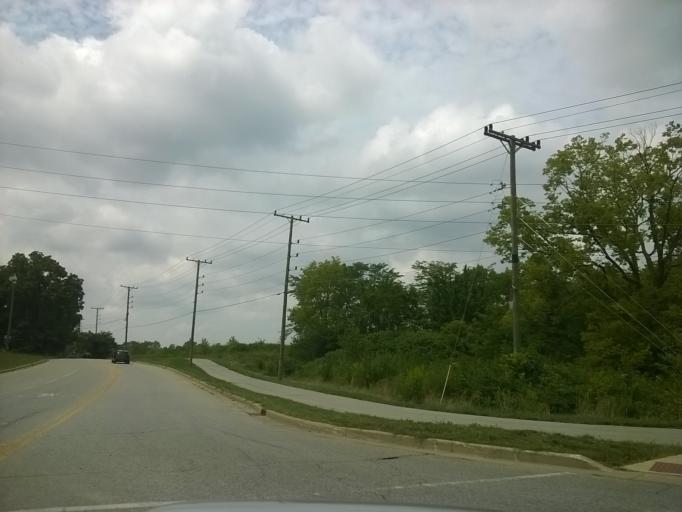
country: US
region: Indiana
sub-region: Hamilton County
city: Carmel
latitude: 39.9413
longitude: -86.0748
